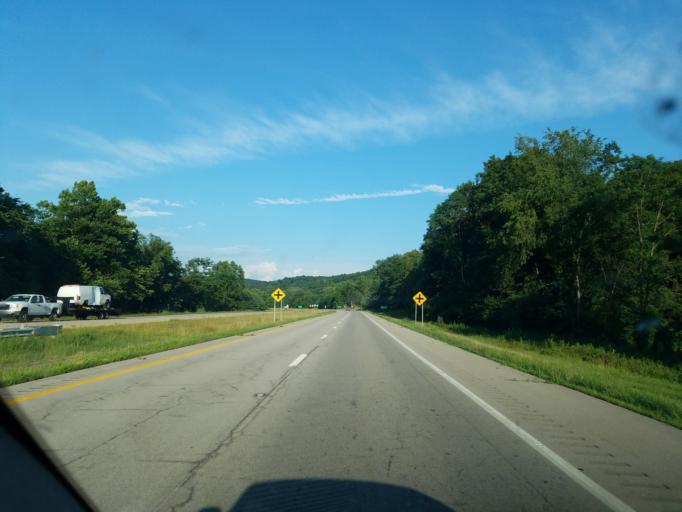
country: US
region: Ohio
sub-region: Pike County
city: Piketon
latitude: 39.0434
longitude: -83.1689
